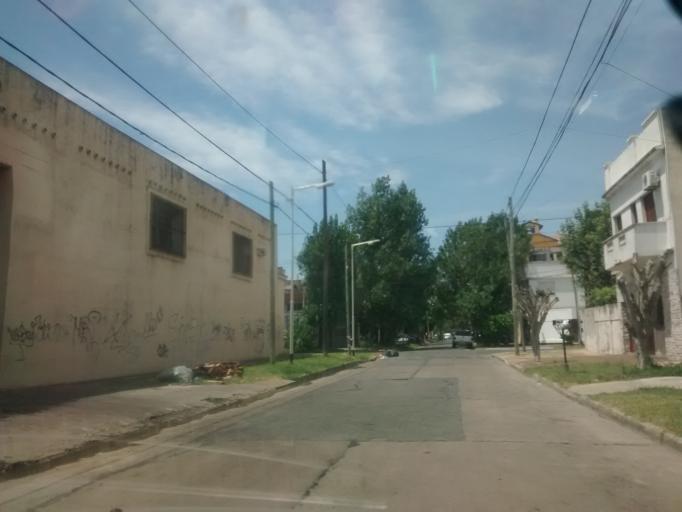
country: AR
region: Buenos Aires
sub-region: Partido de Avellaneda
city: Avellaneda
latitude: -34.6789
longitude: -58.3553
